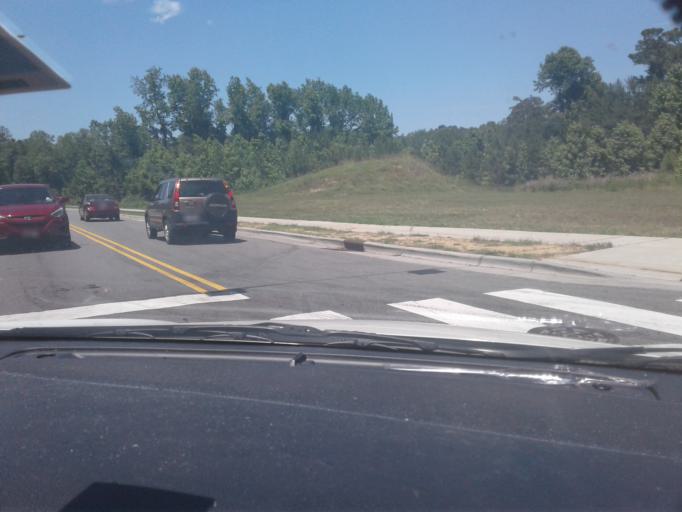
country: US
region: North Carolina
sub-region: Wake County
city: Fuquay-Varina
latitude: 35.5982
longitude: -78.7746
